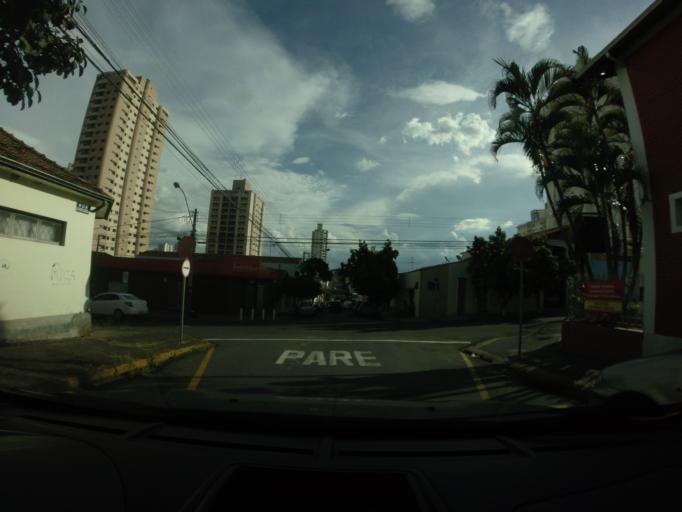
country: BR
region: Sao Paulo
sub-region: Piracicaba
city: Piracicaba
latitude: -22.7251
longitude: -47.6401
